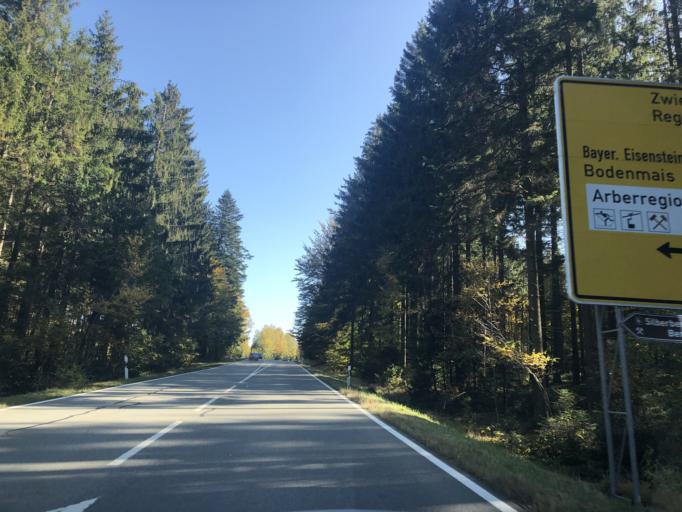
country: DE
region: Bavaria
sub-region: Lower Bavaria
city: Bodenmais
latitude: 49.0528
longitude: 13.1061
